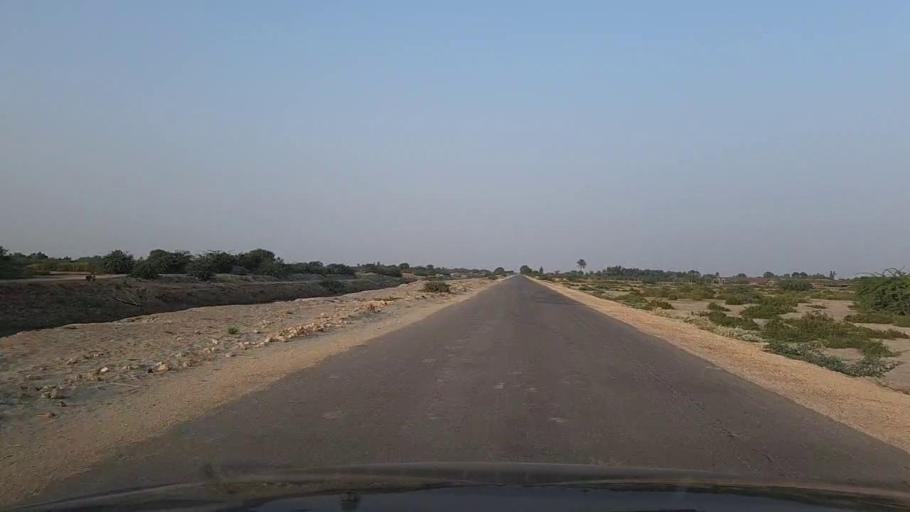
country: PK
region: Sindh
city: Mirpur Sakro
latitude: 24.4913
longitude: 67.8097
